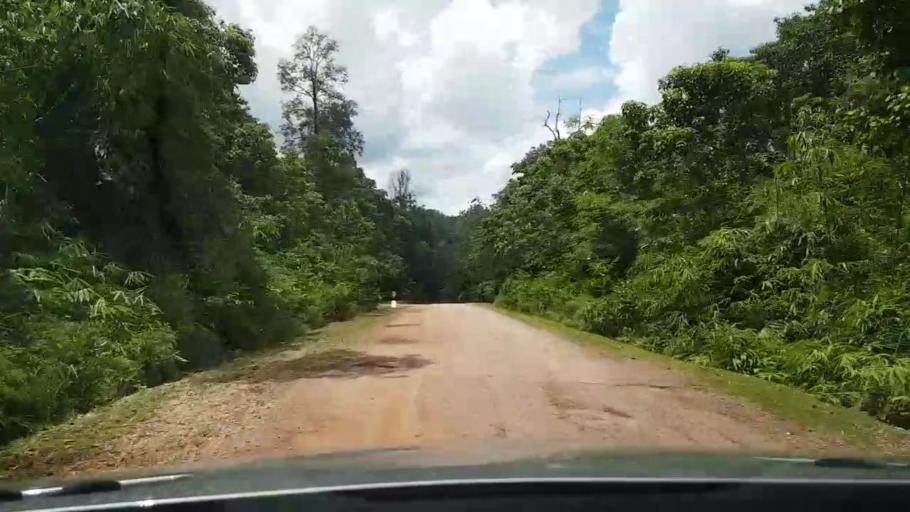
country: MY
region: Pahang
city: Pekan
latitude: 3.1422
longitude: 102.9711
